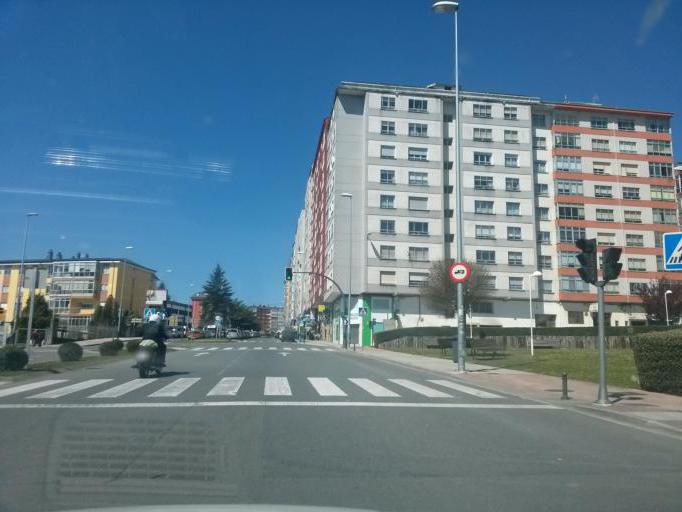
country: ES
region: Galicia
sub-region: Provincia de Lugo
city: Lugo
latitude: 42.9994
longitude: -7.5475
